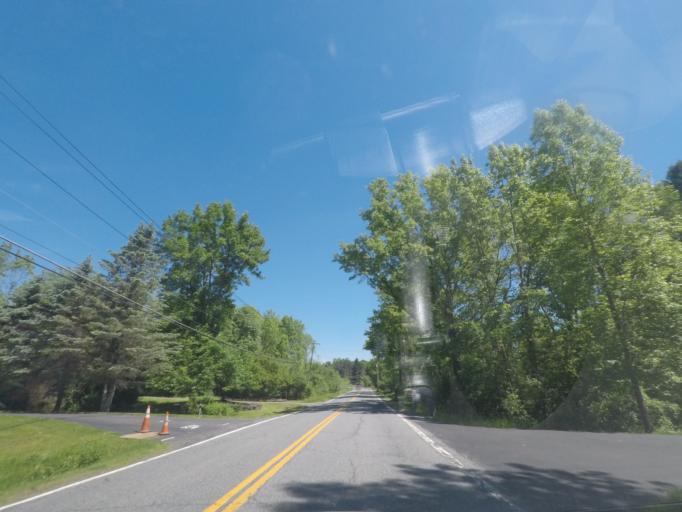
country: US
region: New York
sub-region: Saratoga County
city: Country Knolls
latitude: 42.8904
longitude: -73.8626
